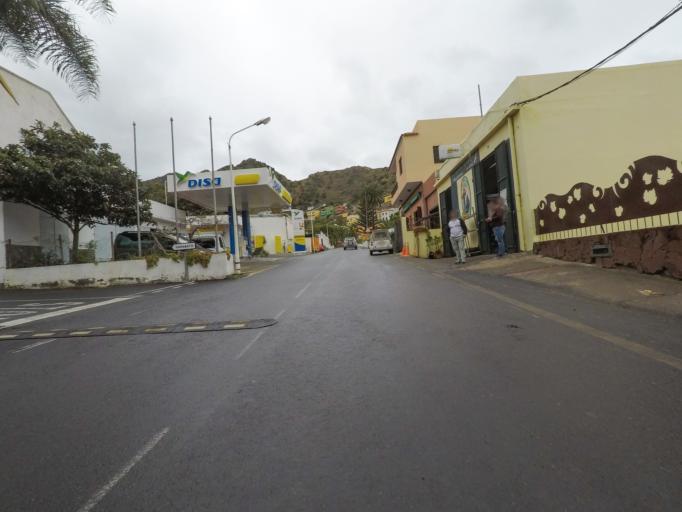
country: ES
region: Canary Islands
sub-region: Provincia de Santa Cruz de Tenerife
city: Vallehermosa
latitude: 28.1791
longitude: -17.2647
